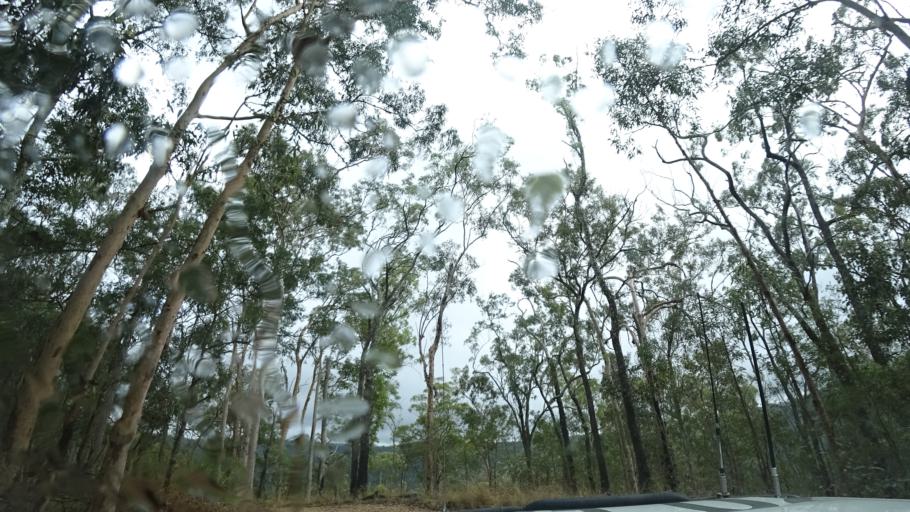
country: AU
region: Queensland
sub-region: Brisbane
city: Pullenvale
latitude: -27.4580
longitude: 152.8457
